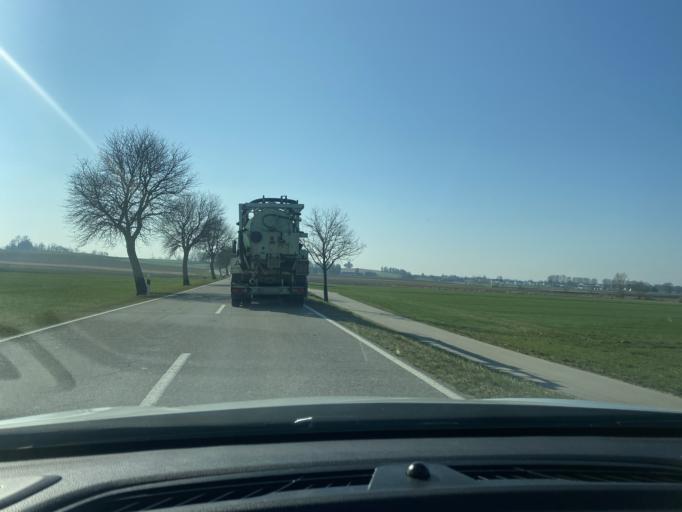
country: DE
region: Bavaria
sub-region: Upper Bavaria
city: Oberding
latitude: 48.2982
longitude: 11.8475
